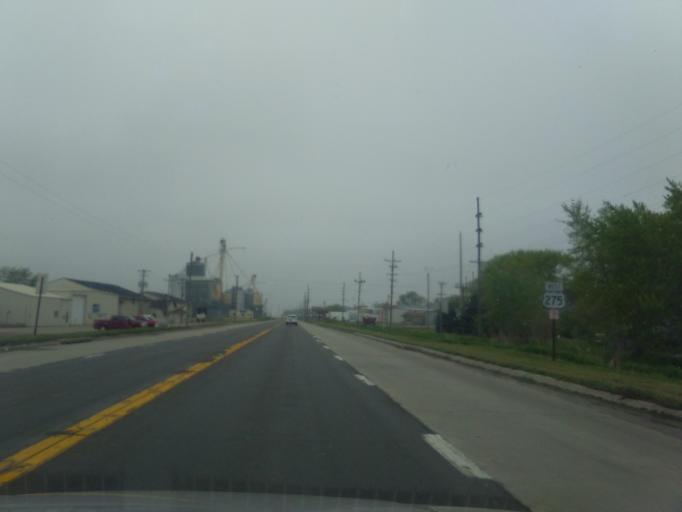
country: US
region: Nebraska
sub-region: Cuming County
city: Wisner
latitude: 41.9262
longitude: -96.8078
